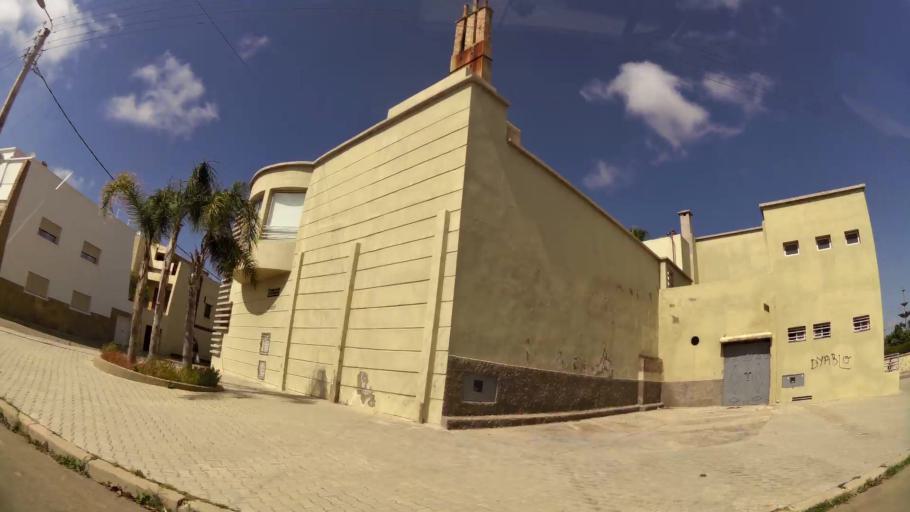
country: MA
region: Rabat-Sale-Zemmour-Zaer
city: Sale
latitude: 34.0389
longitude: -6.7903
